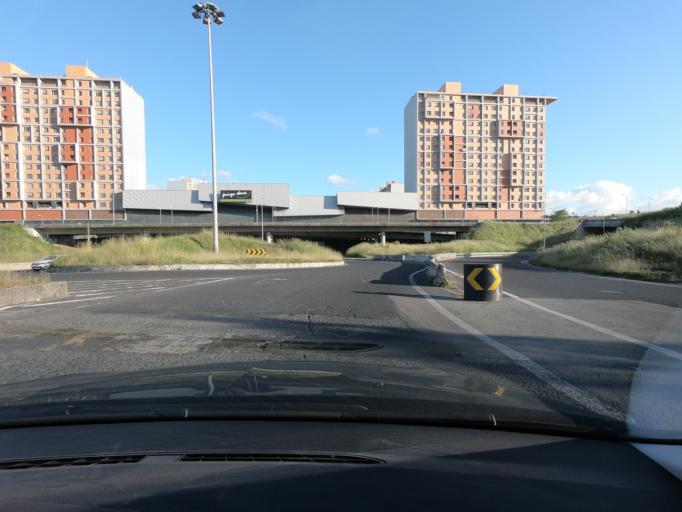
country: PT
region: Lisbon
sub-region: Loures
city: Moscavide
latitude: 38.7513
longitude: -9.1183
